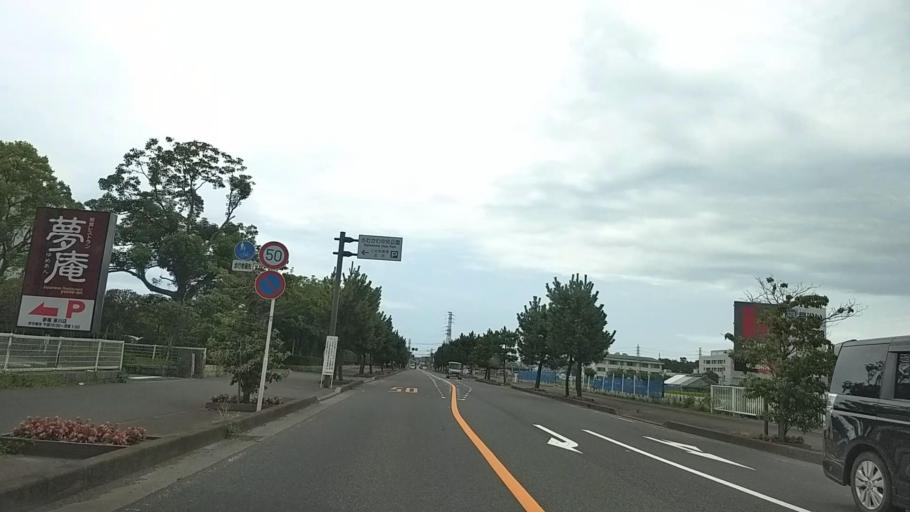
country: JP
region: Kanagawa
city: Chigasaki
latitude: 35.3762
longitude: 139.3843
